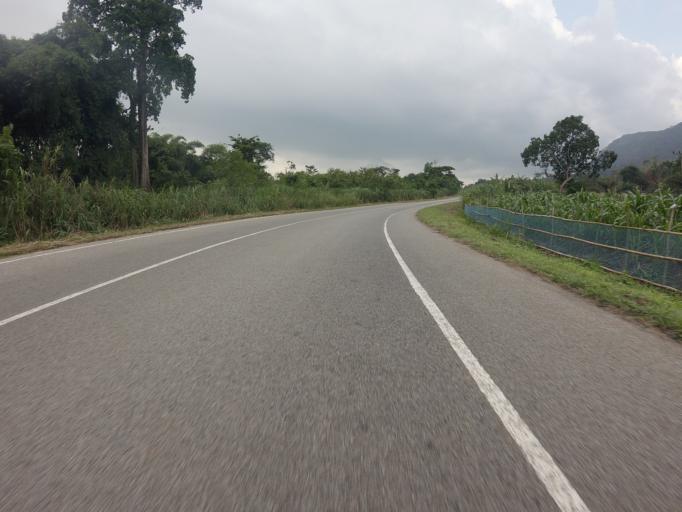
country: GH
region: Volta
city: Ho
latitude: 6.7610
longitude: 0.4794
